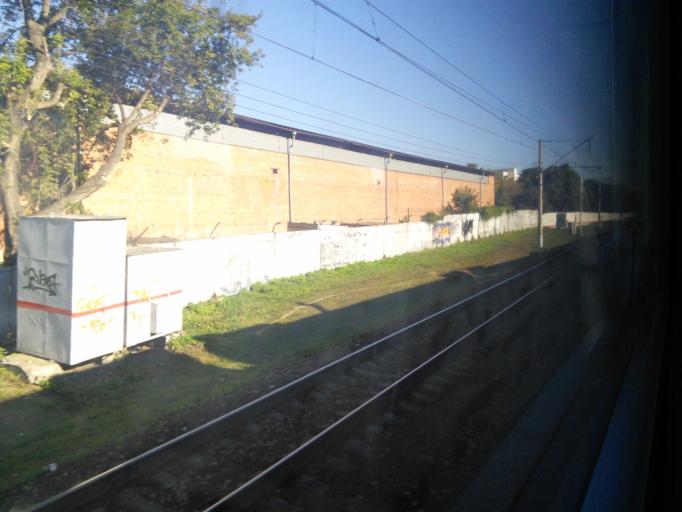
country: RU
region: Moscow
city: Mar'ino
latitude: 55.6719
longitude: 37.7268
